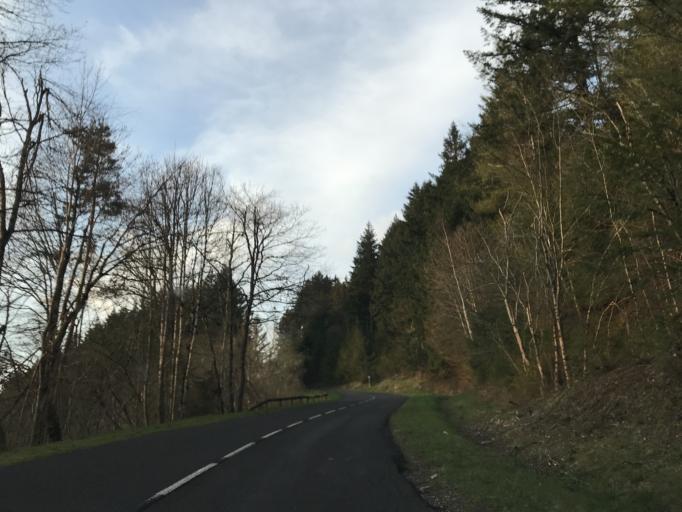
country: FR
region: Auvergne
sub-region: Departement du Puy-de-Dome
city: La Monnerie-le-Montel
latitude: 45.8719
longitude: 3.5896
